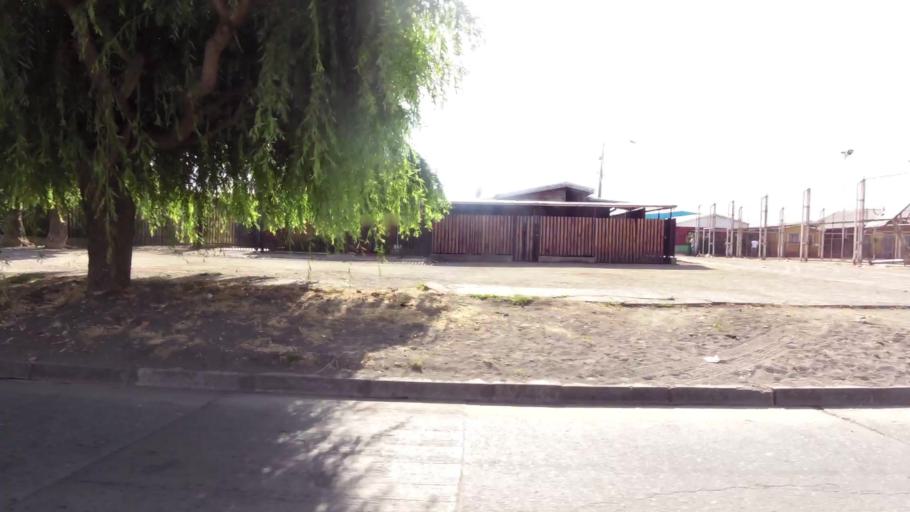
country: CL
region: Biobio
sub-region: Provincia de Concepcion
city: Talcahuano
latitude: -36.7875
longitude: -73.1120
